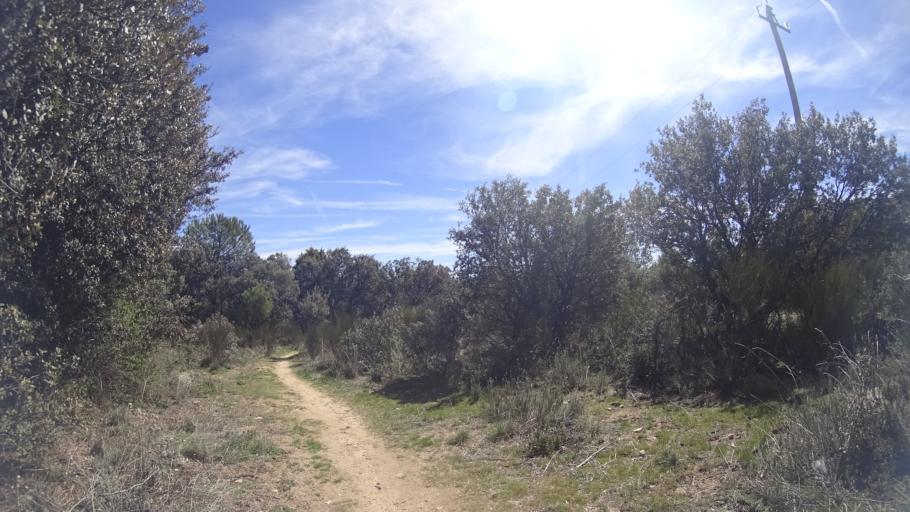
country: ES
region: Madrid
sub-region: Provincia de Madrid
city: Galapagar
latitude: 40.5891
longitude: -3.9844
